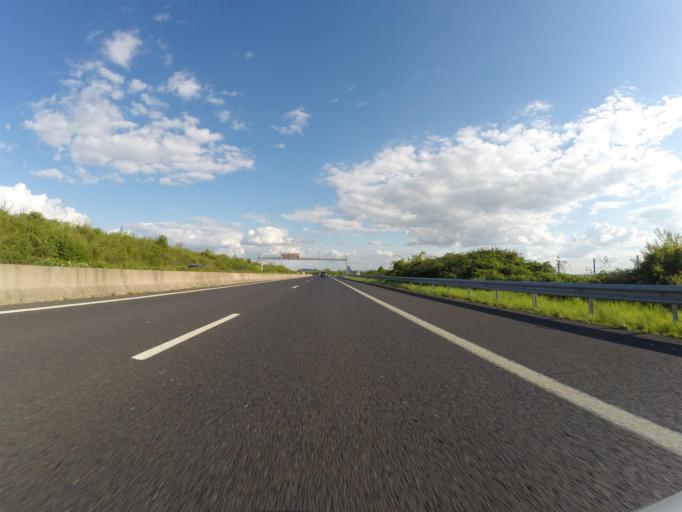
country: LU
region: Grevenmacher
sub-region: Canton de Remich
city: Mondorf-les-Bains
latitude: 49.5045
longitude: 6.3042
